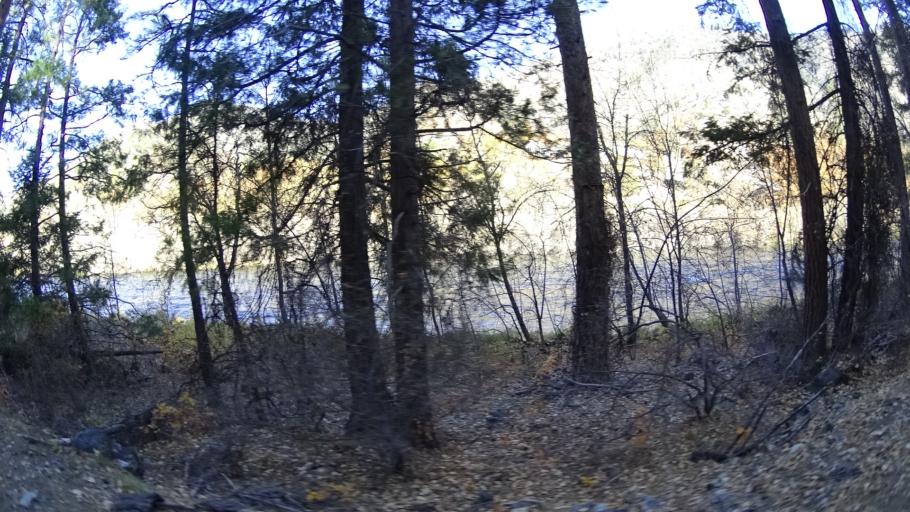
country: US
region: California
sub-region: Siskiyou County
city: Yreka
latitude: 41.8631
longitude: -122.7890
